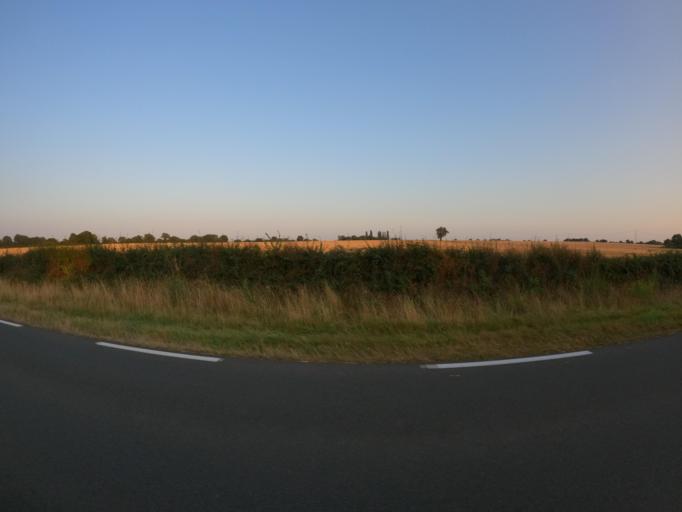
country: FR
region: Pays de la Loire
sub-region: Departement de la Mayenne
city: Meslay-du-Maine
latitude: 47.8615
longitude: -0.5768
